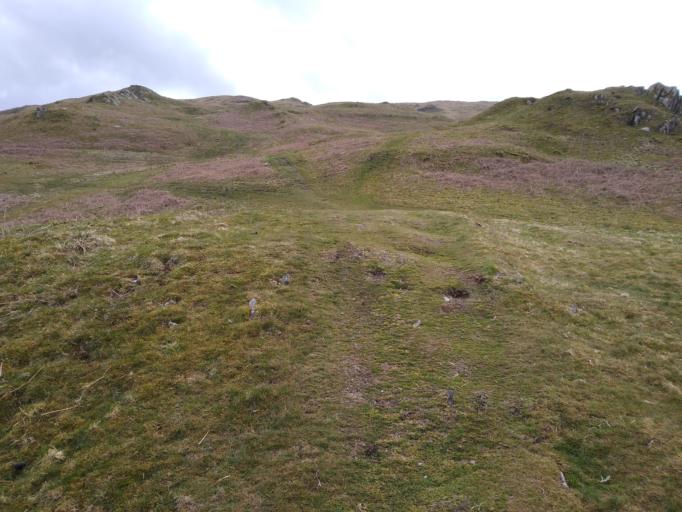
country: GB
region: England
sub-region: Cumbria
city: Windermere
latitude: 54.4171
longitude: -2.8947
